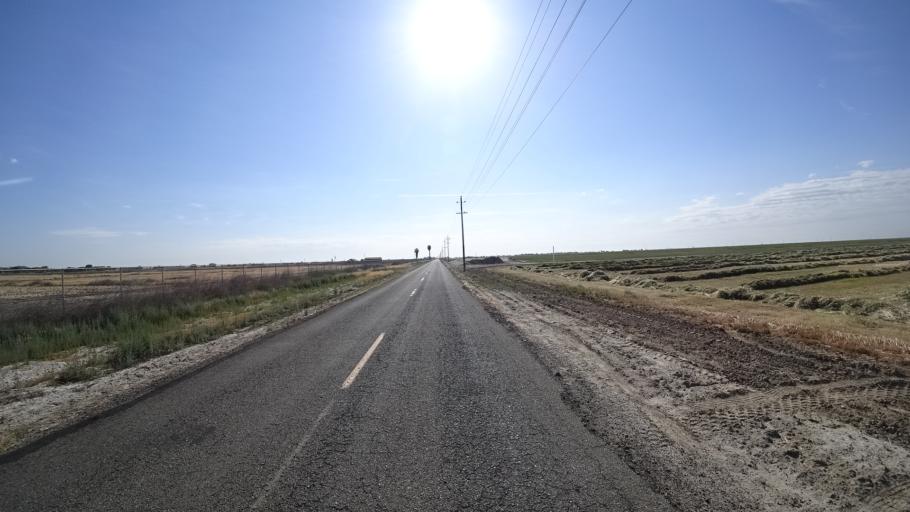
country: US
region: California
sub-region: Kings County
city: Stratford
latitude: 36.2257
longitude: -119.7590
